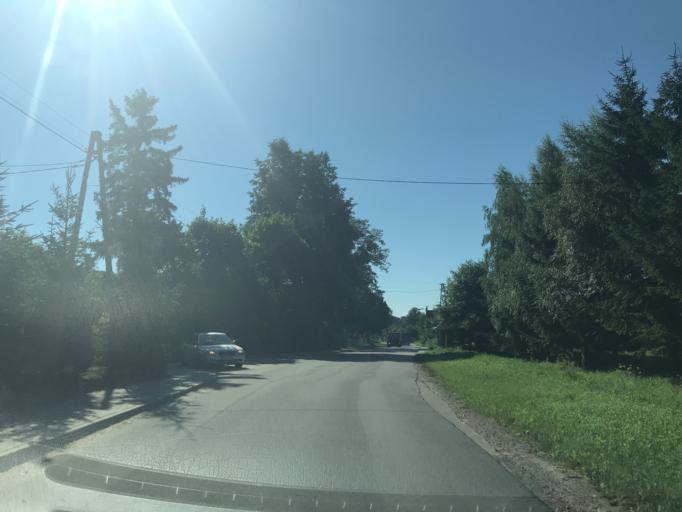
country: PL
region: Warmian-Masurian Voivodeship
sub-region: Powiat ostrodzki
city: Ostroda
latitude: 53.5965
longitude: 19.9012
